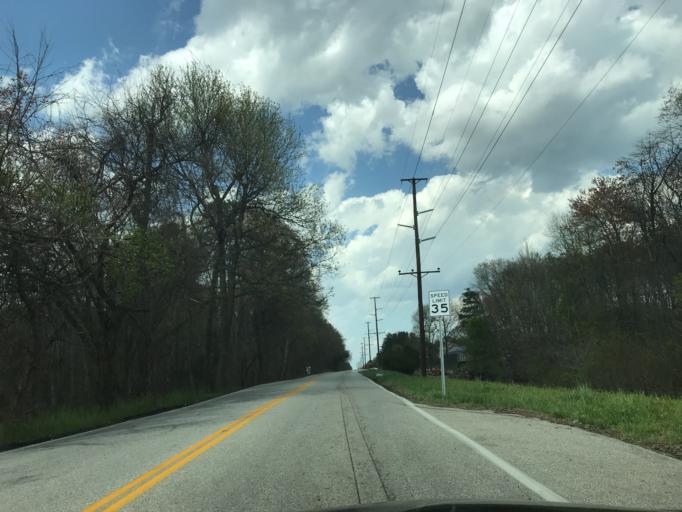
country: US
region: Maryland
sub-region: Anne Arundel County
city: Severn
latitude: 39.1347
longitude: -76.6726
